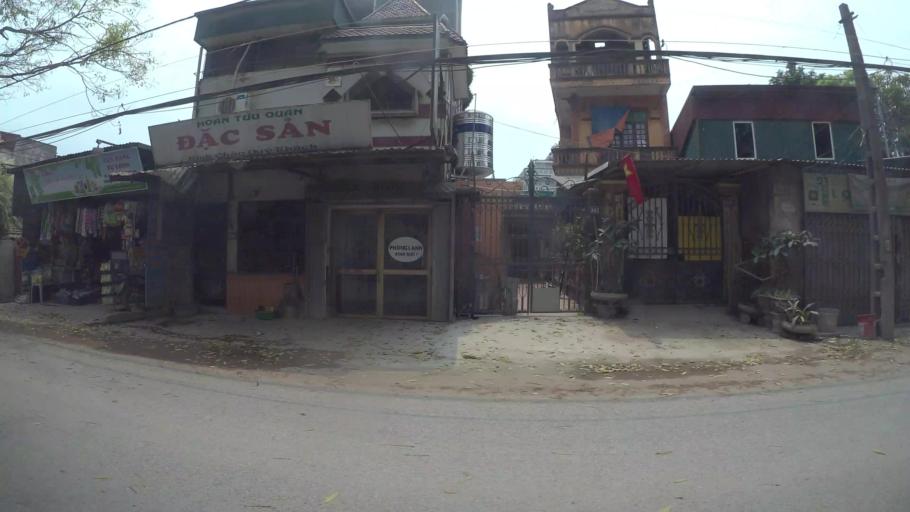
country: VN
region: Ha Noi
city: Cau Dien
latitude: 21.0311
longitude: 105.7394
